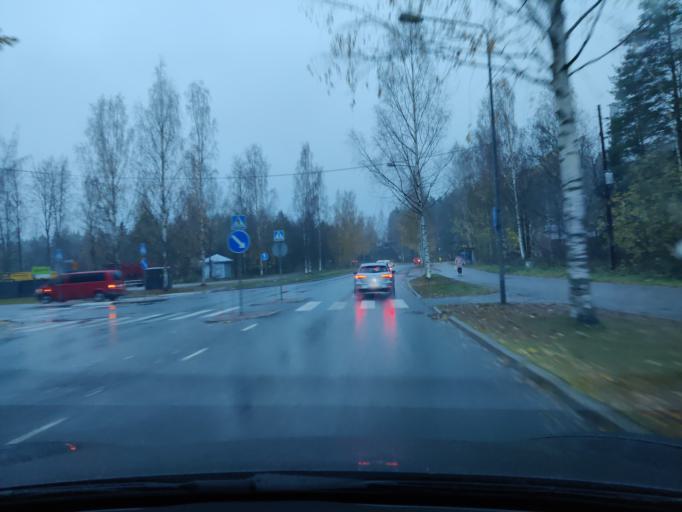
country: FI
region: Northern Savo
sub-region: Kuopio
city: Kuopio
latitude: 62.8498
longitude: 27.6407
